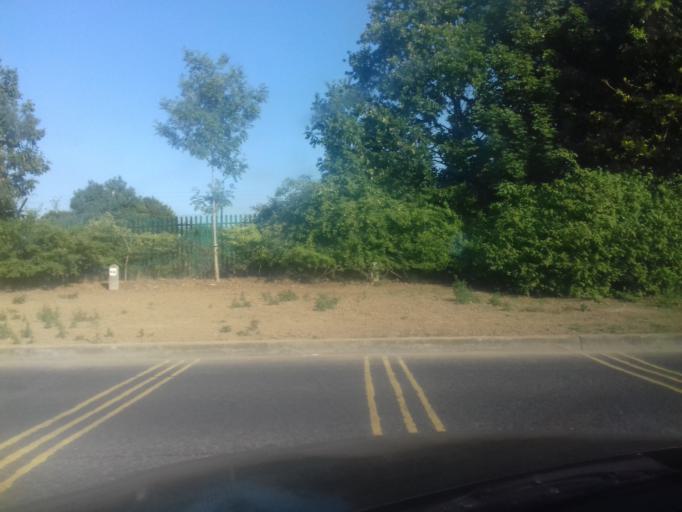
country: IE
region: Leinster
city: Hartstown
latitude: 53.4151
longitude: -6.4218
